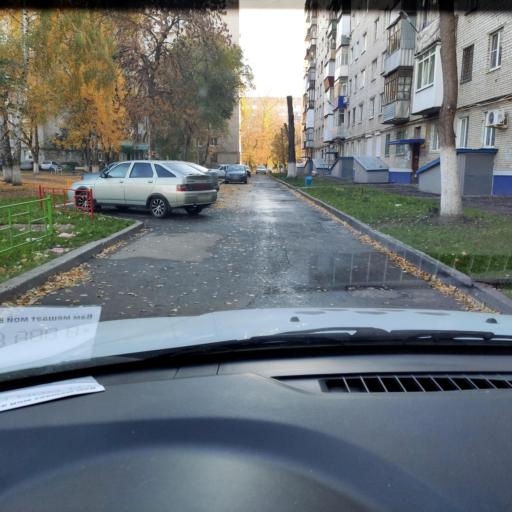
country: RU
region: Samara
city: Tol'yatti
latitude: 53.5101
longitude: 49.4280
